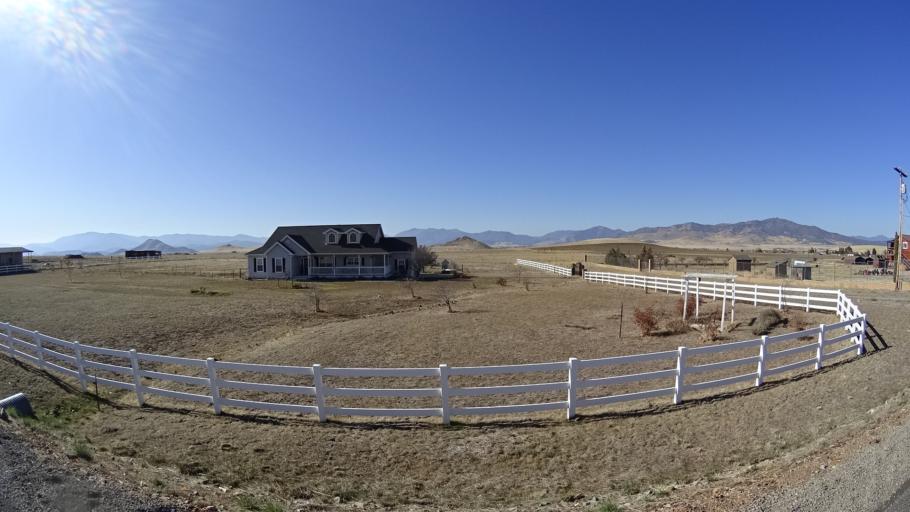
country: US
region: California
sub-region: Siskiyou County
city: Montague
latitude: 41.7497
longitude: -122.4572
